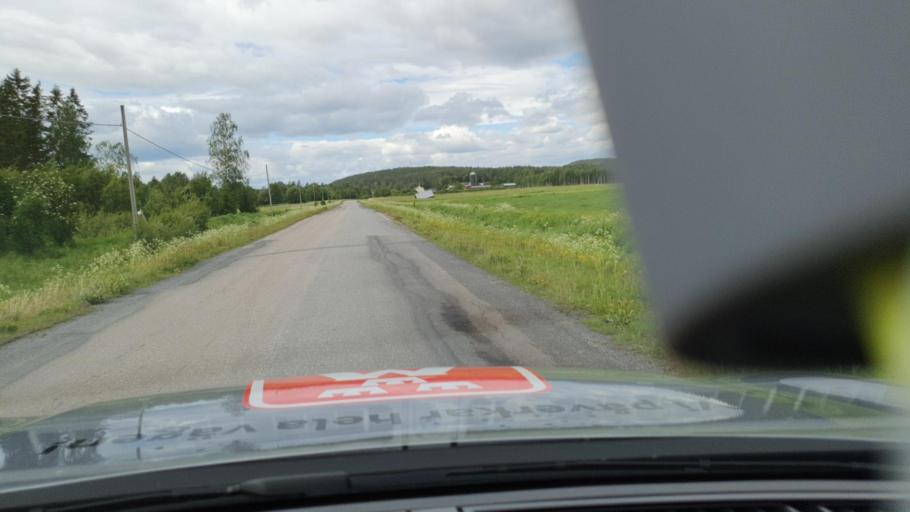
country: SE
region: Norrbotten
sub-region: Bodens Kommun
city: Saevast
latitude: 65.8643
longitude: 21.9061
